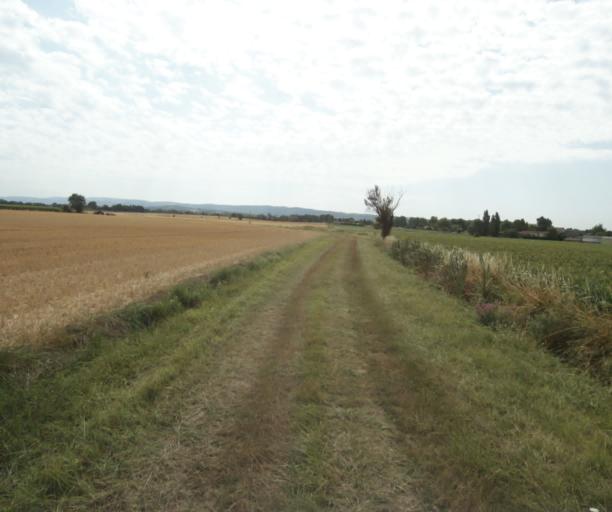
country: FR
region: Midi-Pyrenees
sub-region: Departement de la Haute-Garonne
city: Saint-Felix-Lauragais
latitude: 43.4519
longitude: 1.9245
